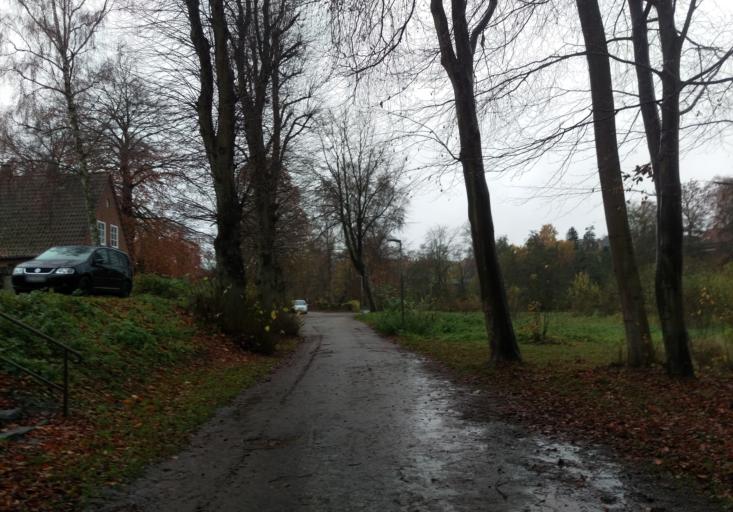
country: DE
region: Schleswig-Holstein
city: Oldenburg in Holstein
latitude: 54.2949
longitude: 10.8831
